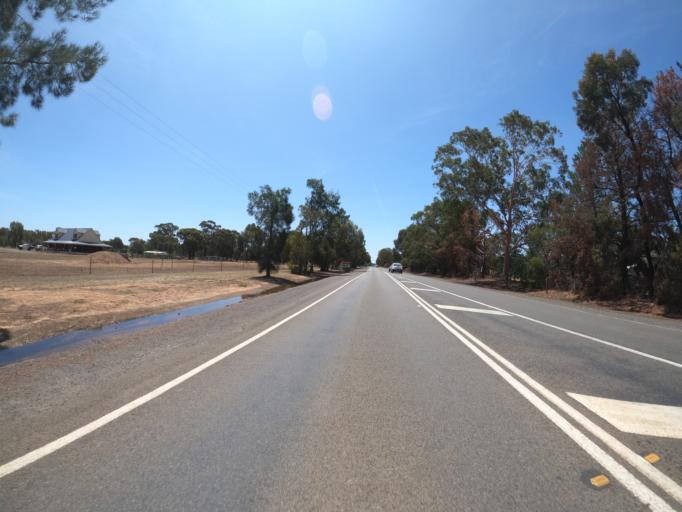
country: AU
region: Victoria
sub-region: Moira
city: Yarrawonga
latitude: -36.0399
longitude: 145.9954
